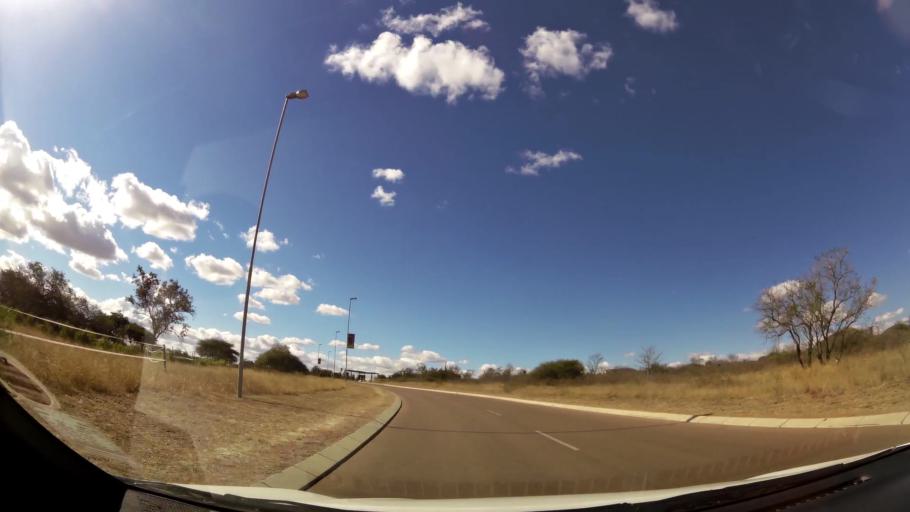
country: ZA
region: Limpopo
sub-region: Capricorn District Municipality
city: Polokwane
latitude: -23.8707
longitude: 29.4954
